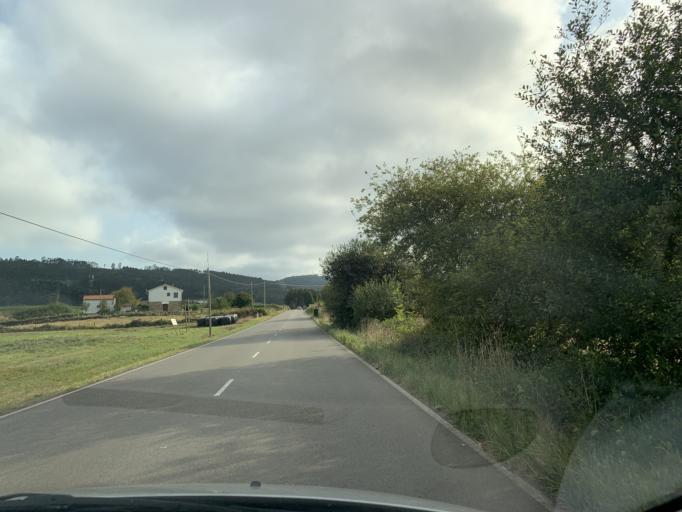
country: ES
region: Asturias
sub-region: Province of Asturias
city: Villaviciosa
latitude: 43.5253
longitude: -5.4355
